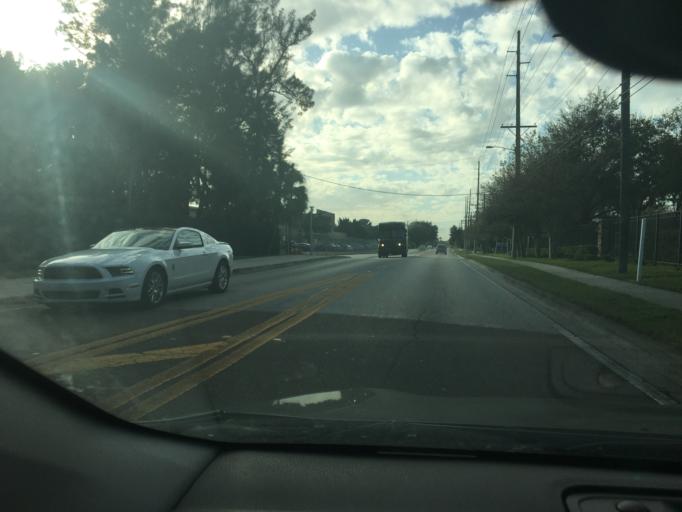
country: US
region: Florida
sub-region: Hillsborough County
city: Temple Terrace
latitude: 28.0436
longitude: -82.4175
